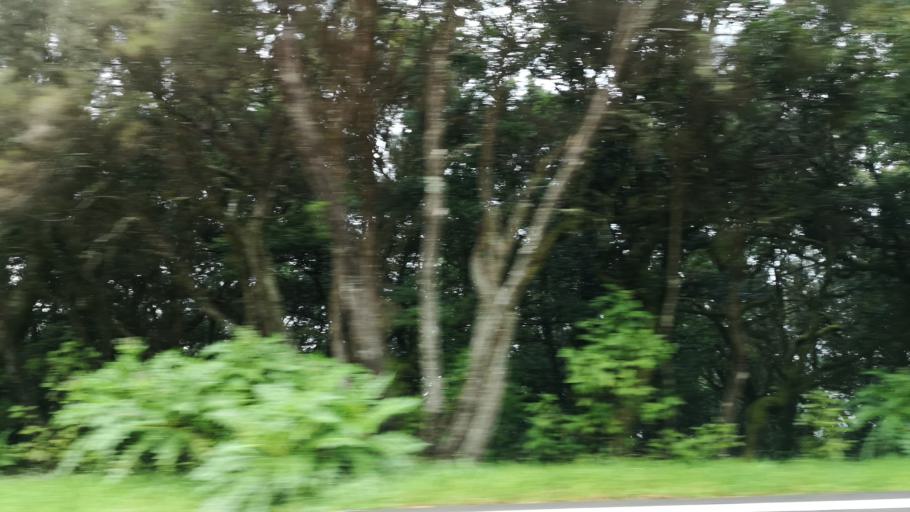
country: ES
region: Canary Islands
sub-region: Provincia de Santa Cruz de Tenerife
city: Alajero
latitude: 28.1164
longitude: -17.2447
